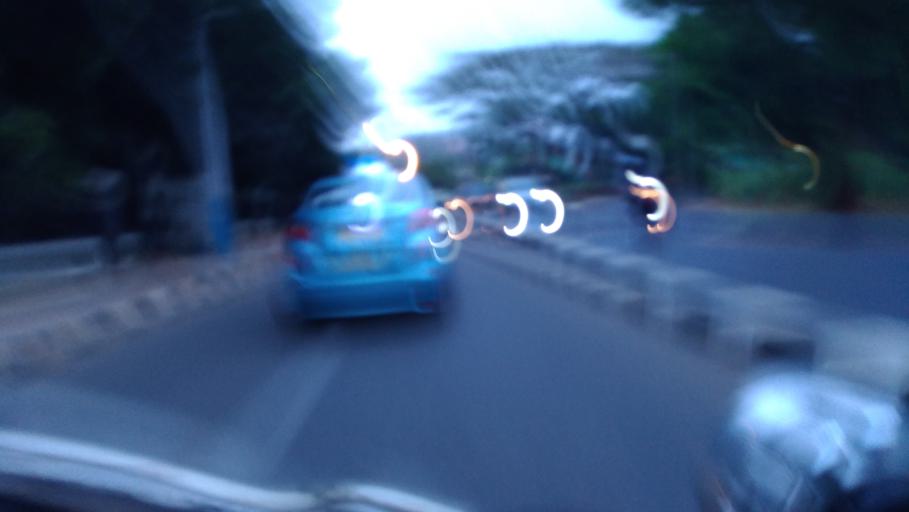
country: ID
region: West Java
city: Cileungsir
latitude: -6.3673
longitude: 106.8892
